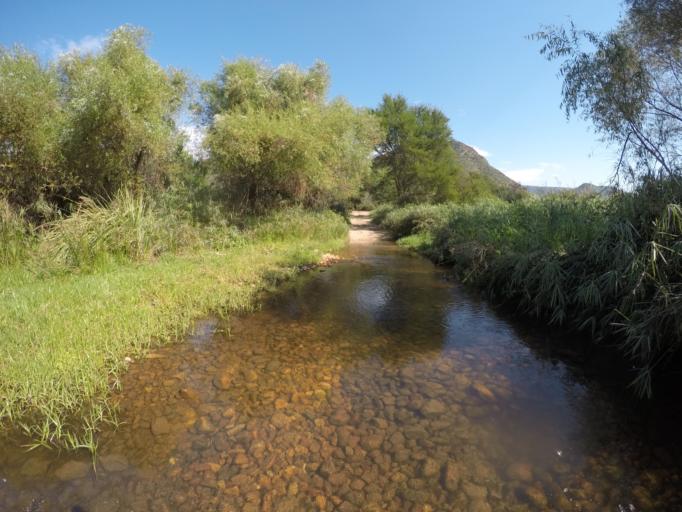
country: ZA
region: Eastern Cape
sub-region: Cacadu District Municipality
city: Kareedouw
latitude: -33.6667
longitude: 24.3846
